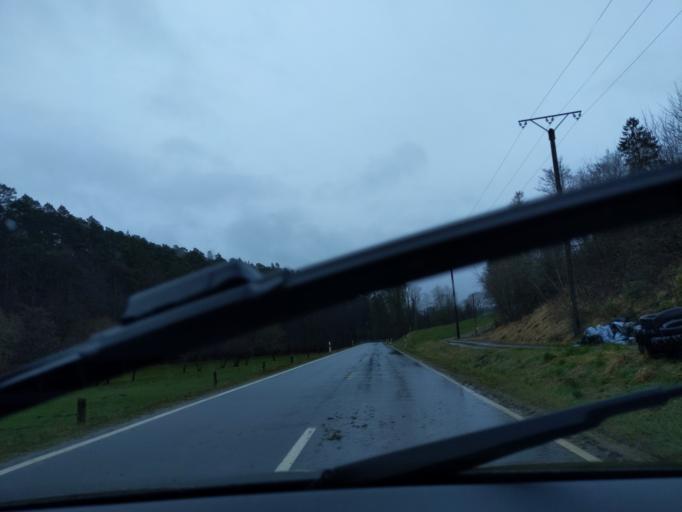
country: DE
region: Hesse
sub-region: Regierungsbezirk Kassel
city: Bad Arolsen
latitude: 51.3342
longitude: 9.0714
